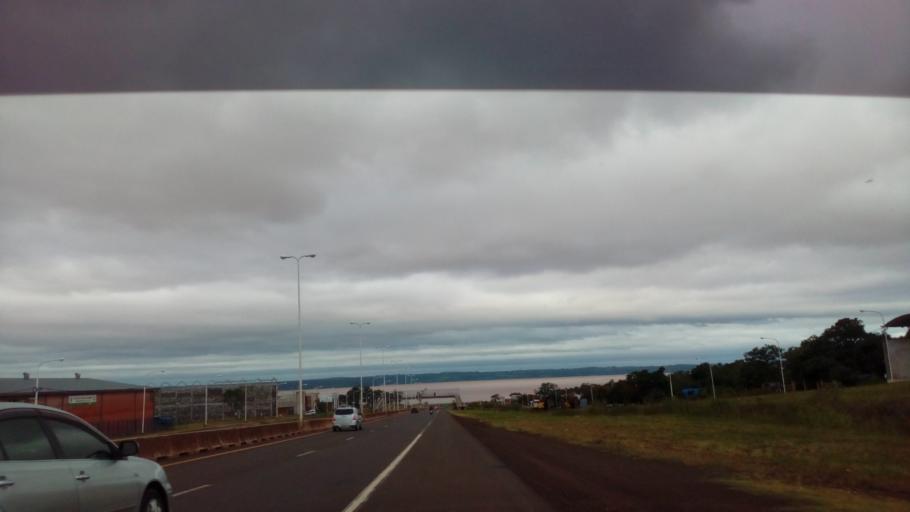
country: AR
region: Misiones
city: Garupa
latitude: -27.4509
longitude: -55.8558
